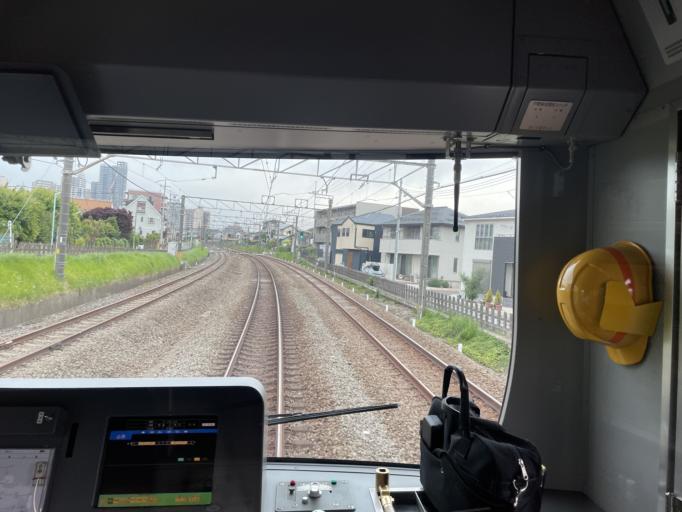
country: JP
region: Saitama
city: Tokorozawa
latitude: 35.7899
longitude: 139.4799
